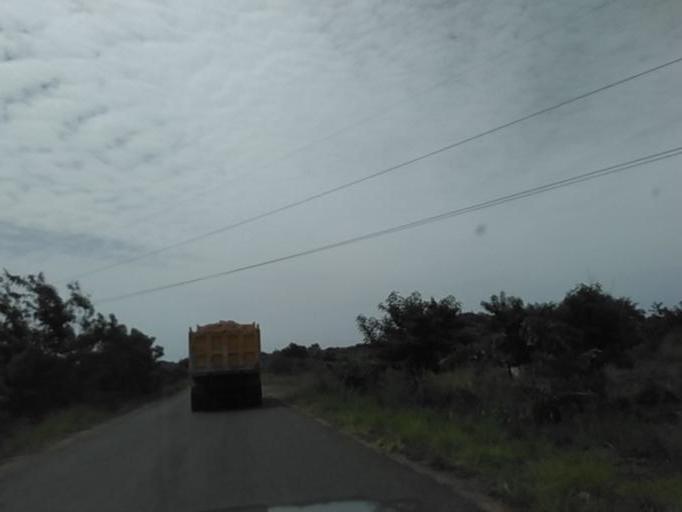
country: GH
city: Akropong
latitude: 6.0953
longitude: 0.0593
